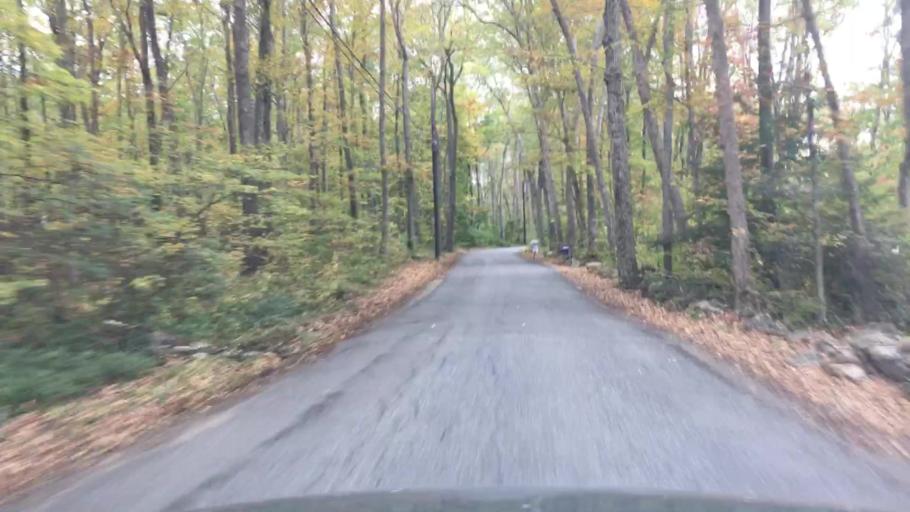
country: US
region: Connecticut
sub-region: Tolland County
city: Storrs
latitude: 41.8810
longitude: -72.1729
